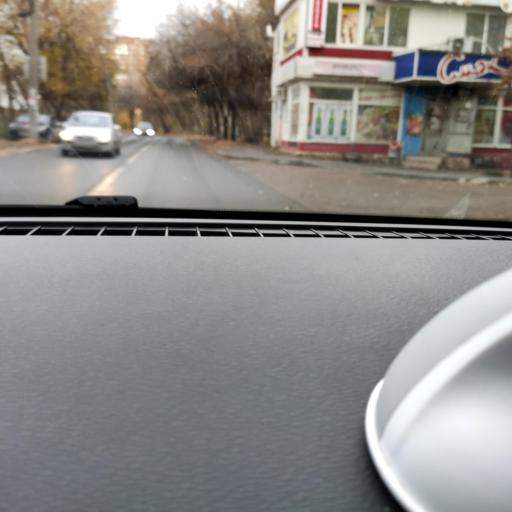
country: RU
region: Samara
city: Samara
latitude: 53.2471
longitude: 50.2190
